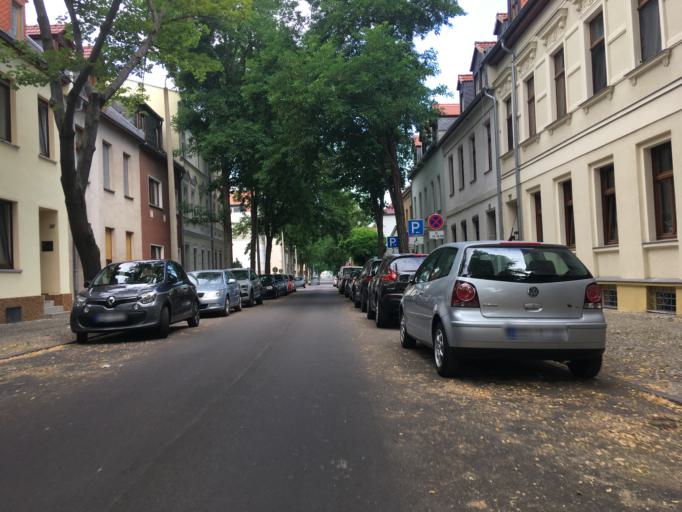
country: DE
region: Saxony-Anhalt
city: Bernburg
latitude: 51.7929
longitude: 11.7484
